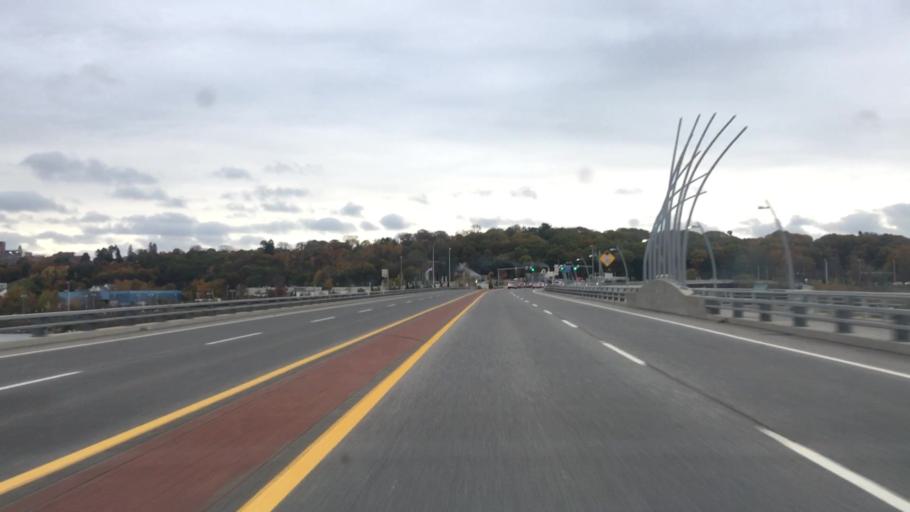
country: US
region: Maine
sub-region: Cumberland County
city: South Portland Gardens
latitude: 43.6434
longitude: -70.2837
